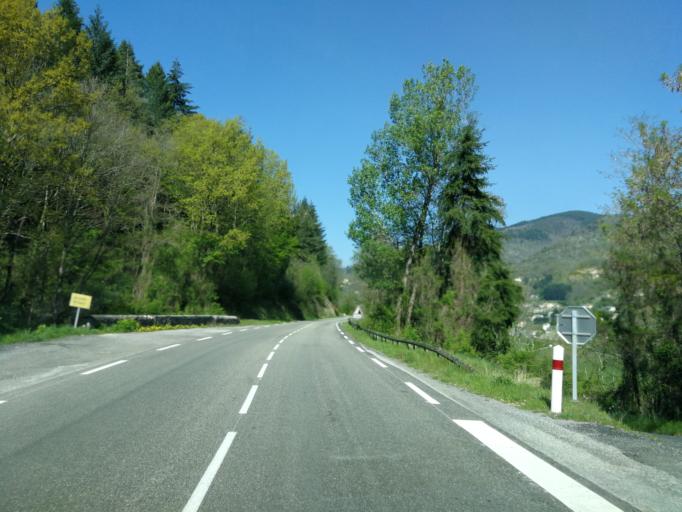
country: FR
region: Rhone-Alpes
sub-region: Departement de l'Ardeche
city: Le Cheylard
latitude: 44.9096
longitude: 4.4512
